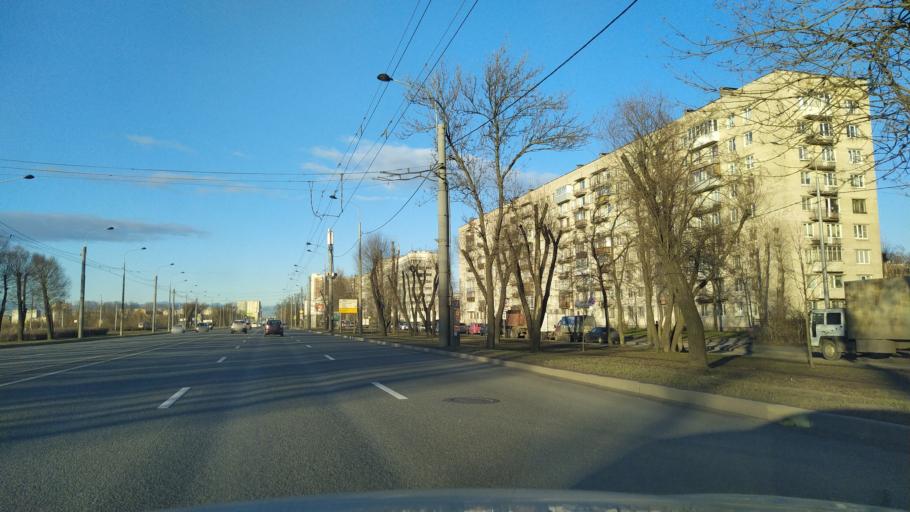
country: RU
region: St.-Petersburg
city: Uritsk
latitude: 59.8348
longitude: 30.1971
